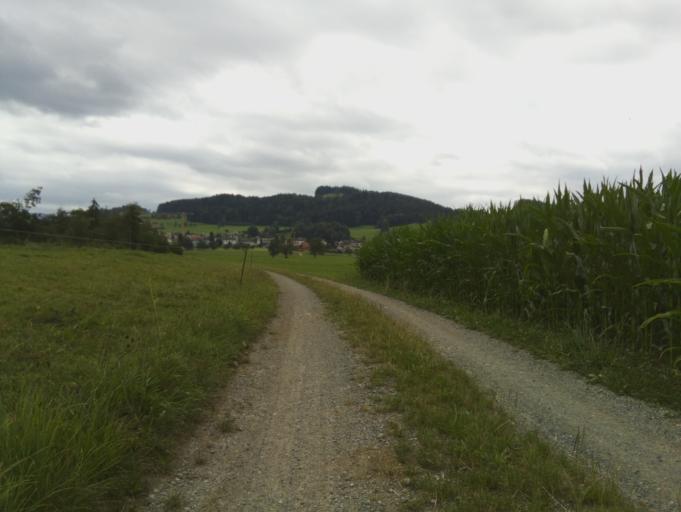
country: CH
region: Saint Gallen
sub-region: Wahlkreis Toggenburg
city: Ganterschwil
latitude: 47.3874
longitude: 9.0877
